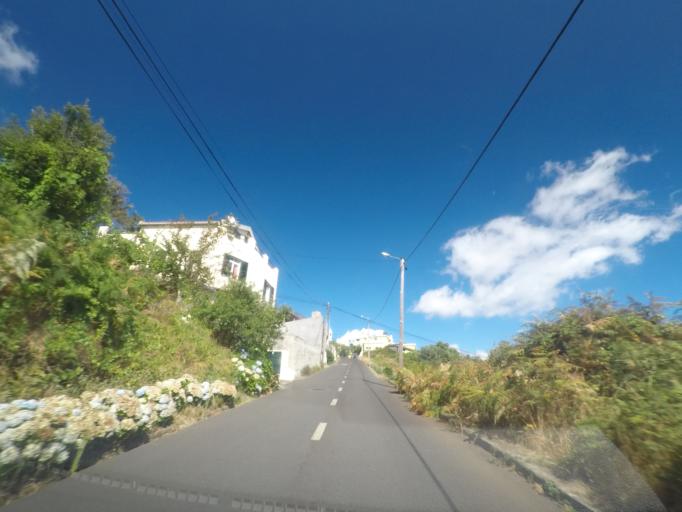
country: PT
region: Madeira
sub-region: Ribeira Brava
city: Campanario
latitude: 32.6946
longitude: -17.0305
